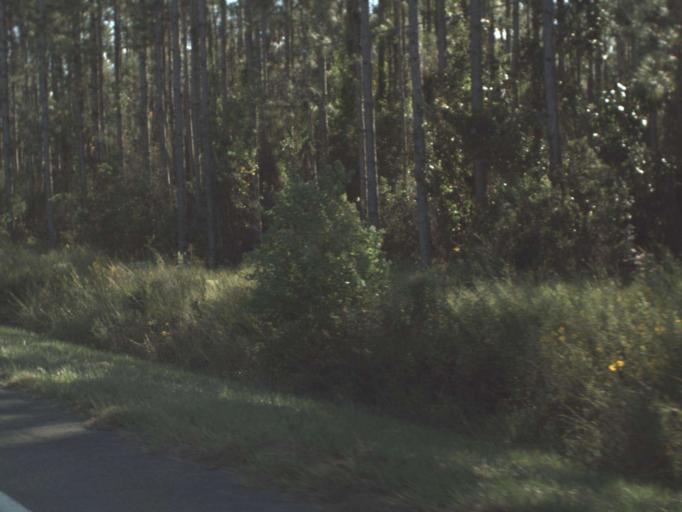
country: US
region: Florida
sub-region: Gulf County
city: Wewahitchka
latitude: 30.0187
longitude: -85.1780
